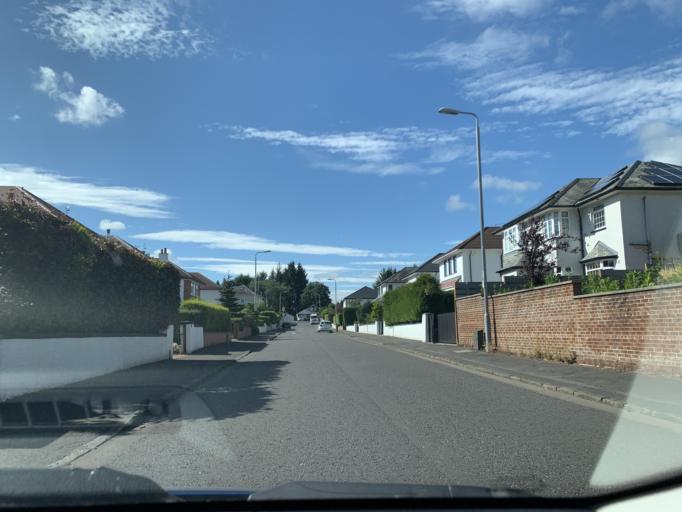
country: GB
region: Scotland
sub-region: East Renfrewshire
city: Newton Mearns
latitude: 55.7781
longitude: -4.3187
